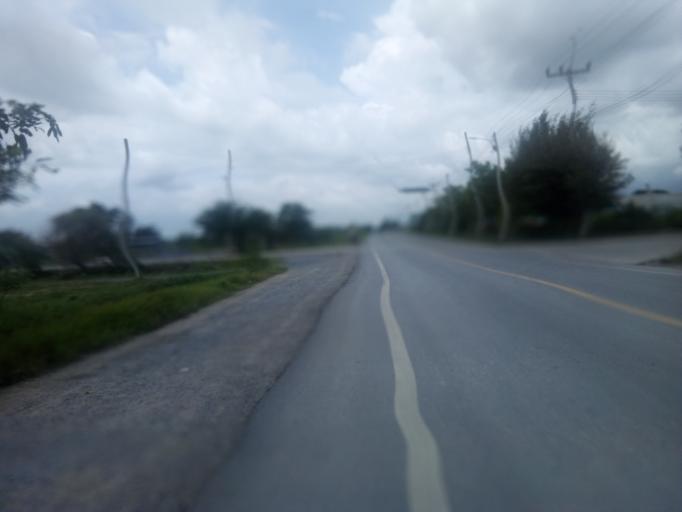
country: TH
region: Pathum Thani
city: Ban Lam Luk Ka
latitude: 14.0057
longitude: 100.8225
